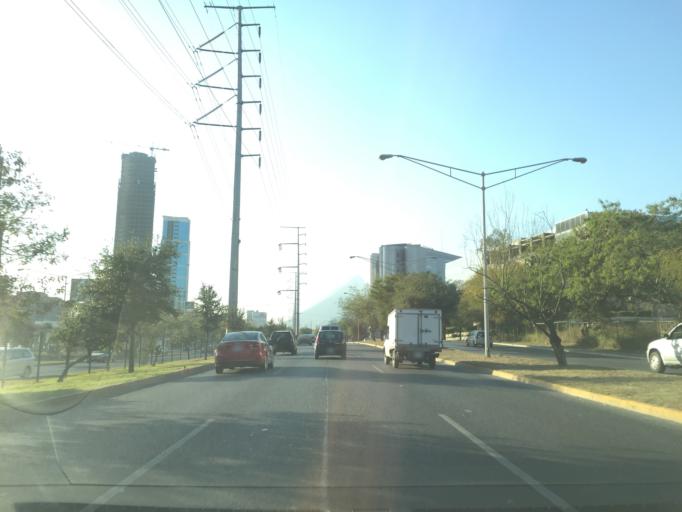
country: MX
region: Nuevo Leon
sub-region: Monterrey
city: Monterrey
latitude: 25.6482
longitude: -100.3278
